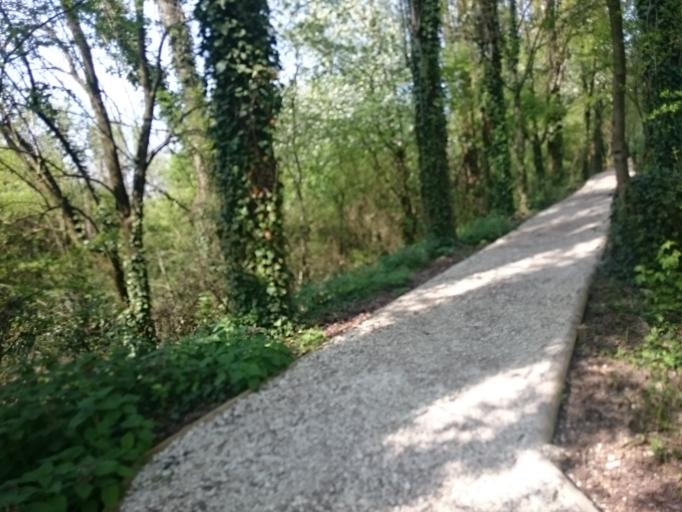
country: IT
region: Veneto
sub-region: Provincia di Padova
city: Bosco
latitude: 45.4393
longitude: 11.7850
